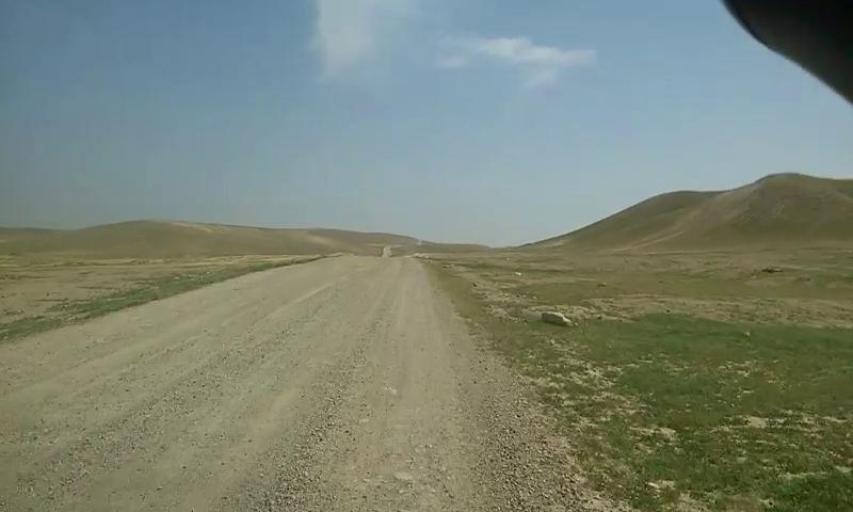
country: PS
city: `Arab ar Rashaydah
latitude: 31.5299
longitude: 35.2882
